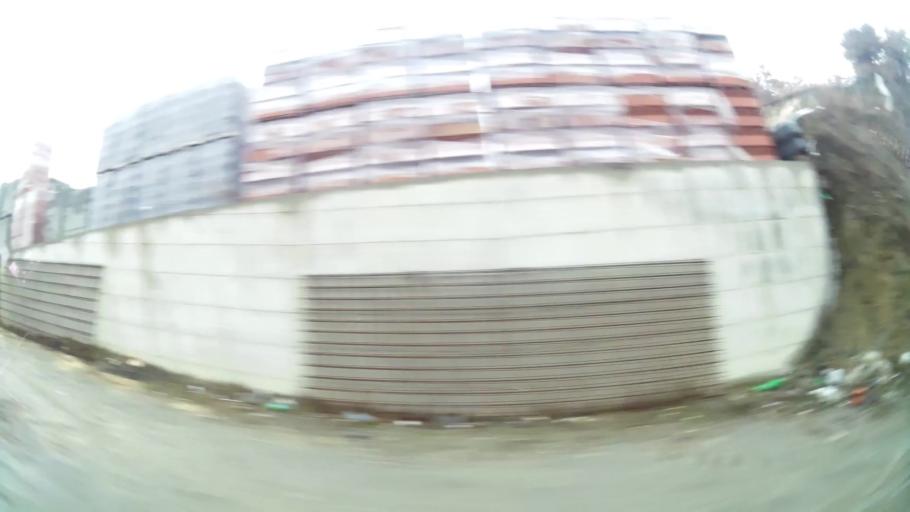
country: XK
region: Ferizaj
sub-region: Hani i Elezit
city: Hani i Elezit
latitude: 42.1738
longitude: 21.2738
